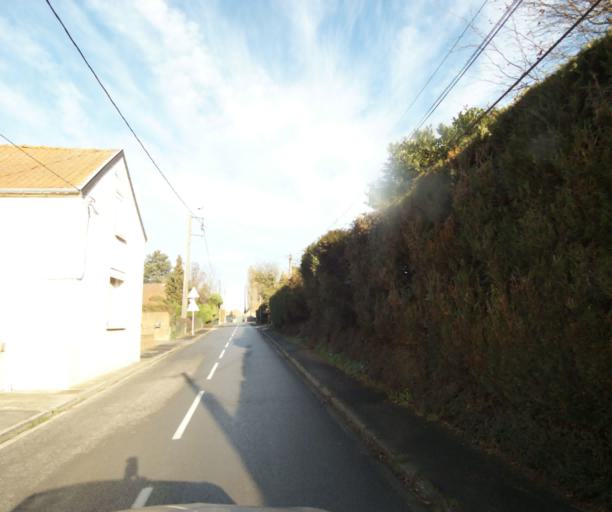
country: FR
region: Nord-Pas-de-Calais
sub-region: Departement du Nord
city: Curgies
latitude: 50.3522
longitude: 3.5978
